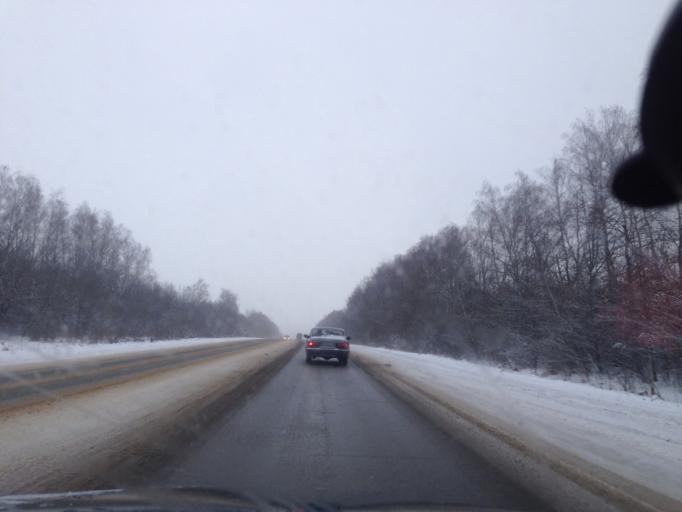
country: RU
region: Tula
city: Bolokhovo
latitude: 54.0969
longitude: 37.7677
